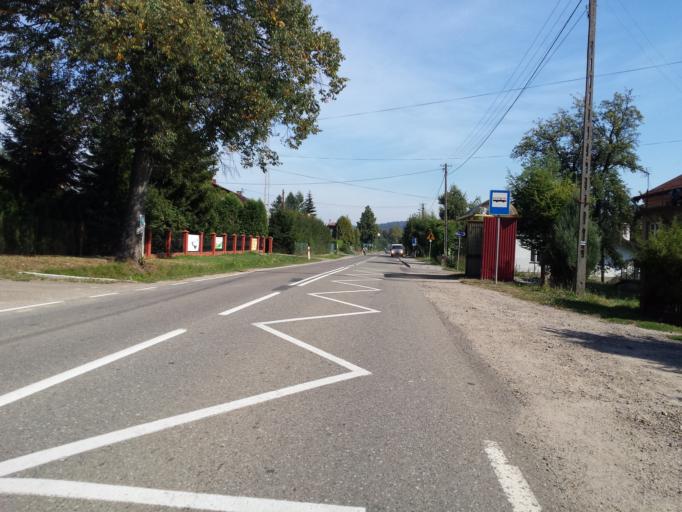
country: PL
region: Subcarpathian Voivodeship
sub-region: Powiat leski
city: Baligrod
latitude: 49.3294
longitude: 22.2850
